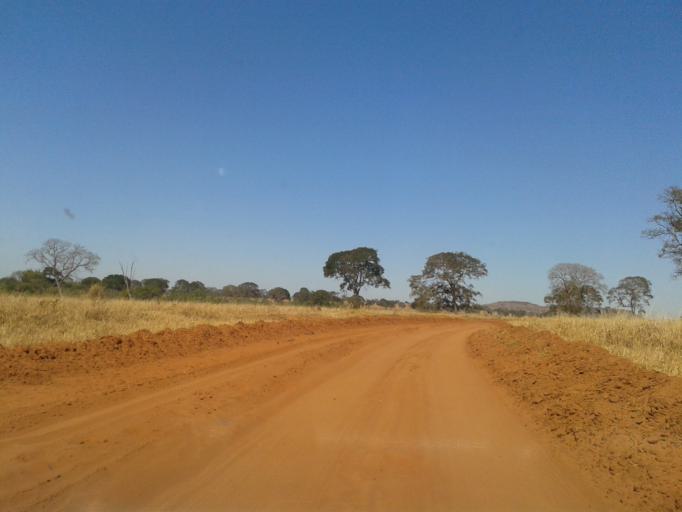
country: BR
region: Minas Gerais
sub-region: Santa Vitoria
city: Santa Vitoria
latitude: -19.1635
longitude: -50.1562
